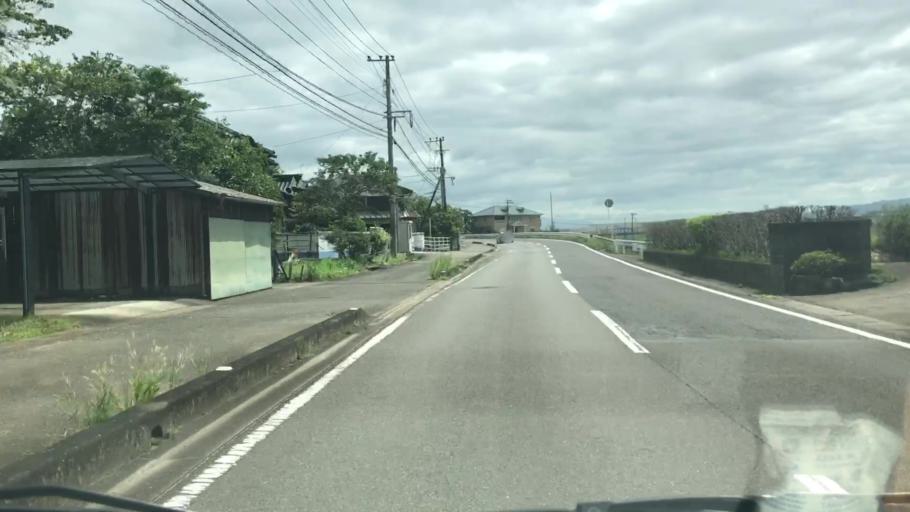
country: JP
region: Saga Prefecture
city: Kashima
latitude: 33.2286
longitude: 130.1532
